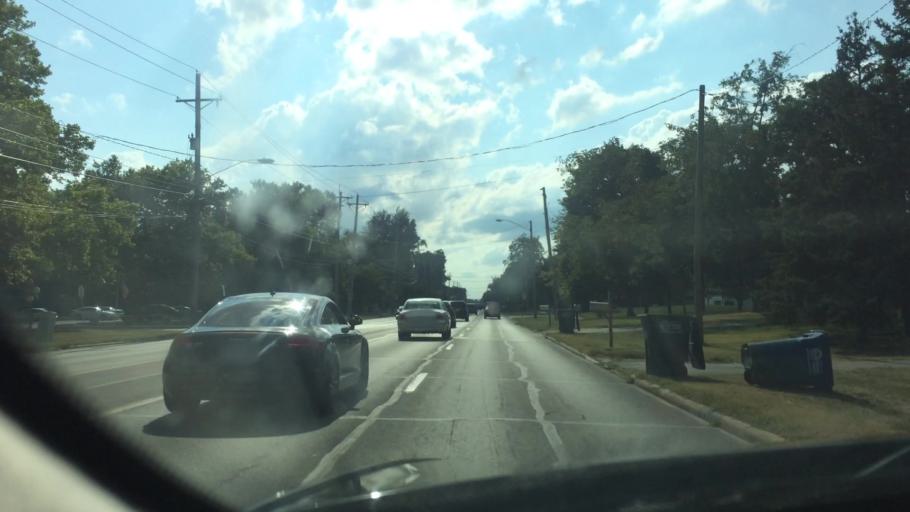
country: US
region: Ohio
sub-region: Lucas County
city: Maumee
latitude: 41.5946
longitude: -83.6564
